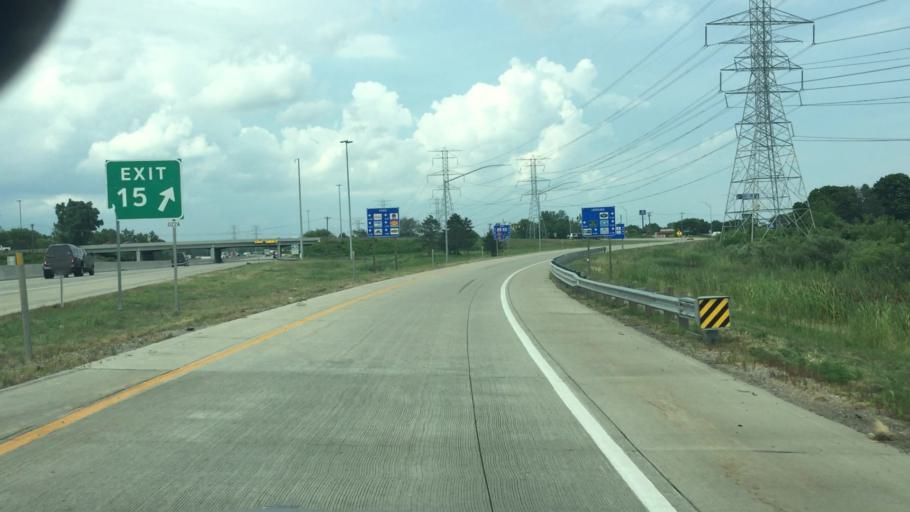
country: US
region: Michigan
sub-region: Monroe County
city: Detroit Beach
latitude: 41.9240
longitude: -83.3604
